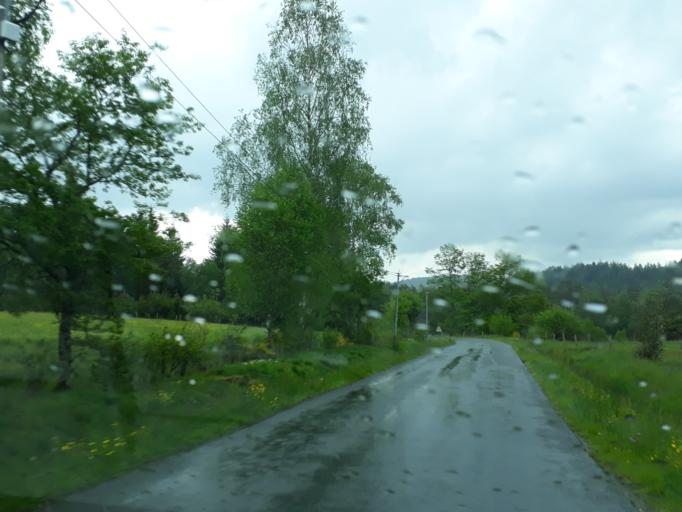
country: FR
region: Limousin
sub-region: Departement de la Haute-Vienne
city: Peyrat-le-Chateau
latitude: 45.8310
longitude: 1.8522
